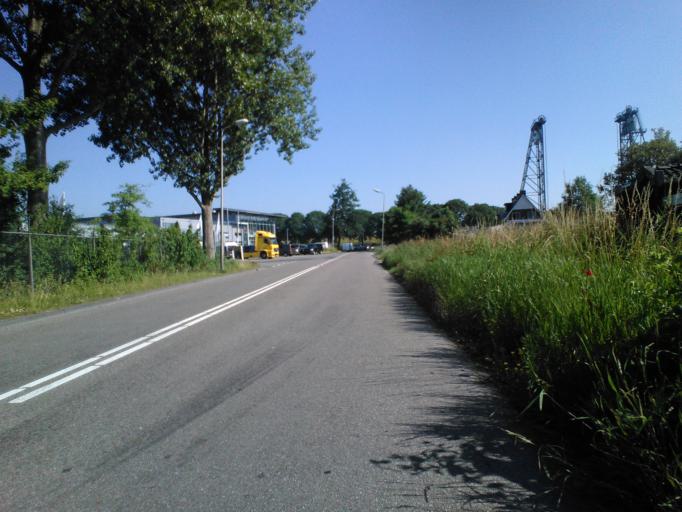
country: NL
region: South Holland
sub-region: Gemeente Alphen aan den Rijn
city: Alphen aan den Rijn
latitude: 52.1161
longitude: 4.6724
